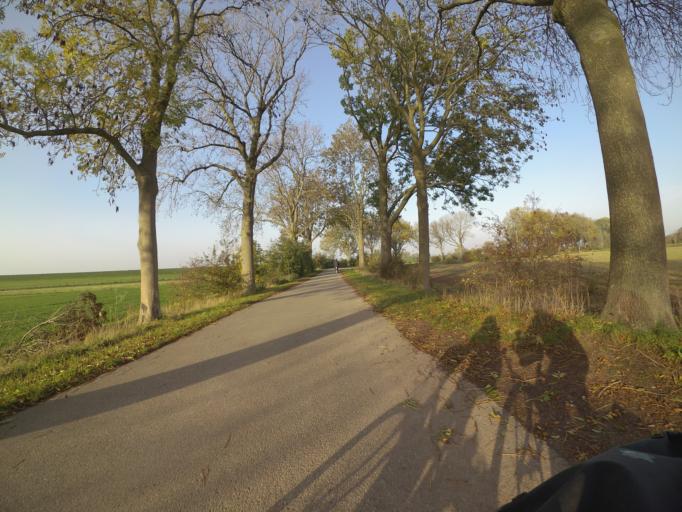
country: NL
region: Gelderland
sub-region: Gemeente Maasdriel
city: Heerewaarden
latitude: 51.8350
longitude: 5.4102
